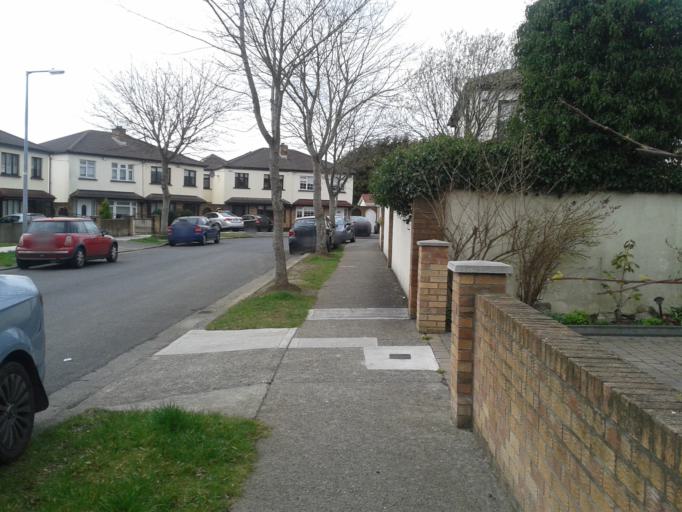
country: IE
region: Leinster
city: Beaumont
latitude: 53.4026
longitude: -6.2377
